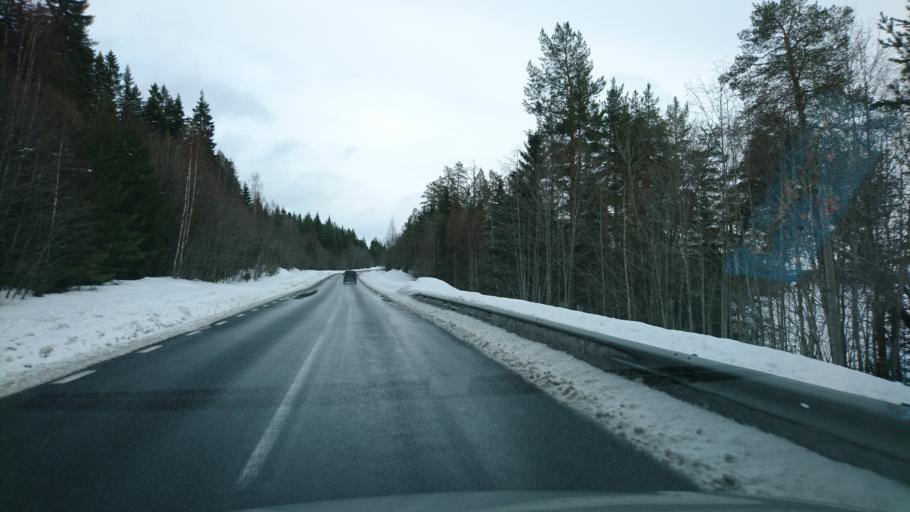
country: SE
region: Vaesternorrland
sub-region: Solleftea Kommun
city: Solleftea
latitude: 63.0561
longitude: 17.0383
